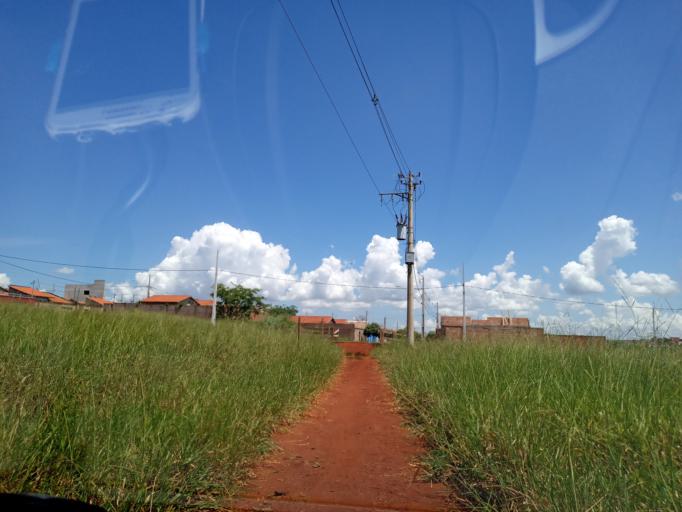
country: BR
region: Goias
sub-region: Itumbiara
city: Itumbiara
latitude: -18.4352
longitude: -49.1789
